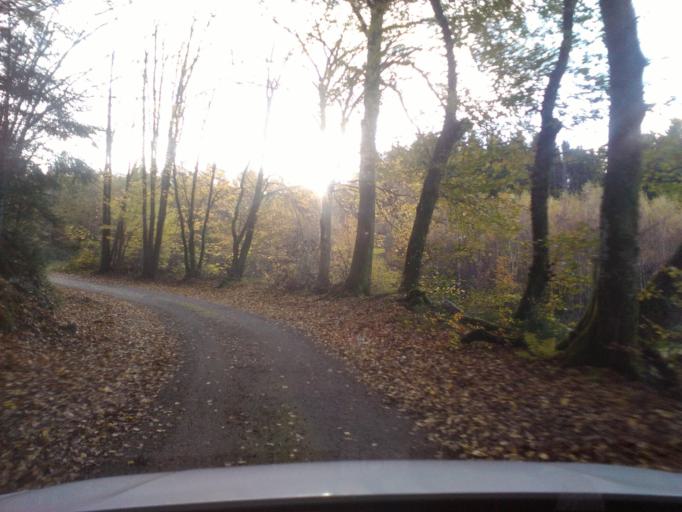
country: FR
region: Lorraine
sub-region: Departement des Vosges
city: Senones
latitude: 48.4137
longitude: 7.0550
